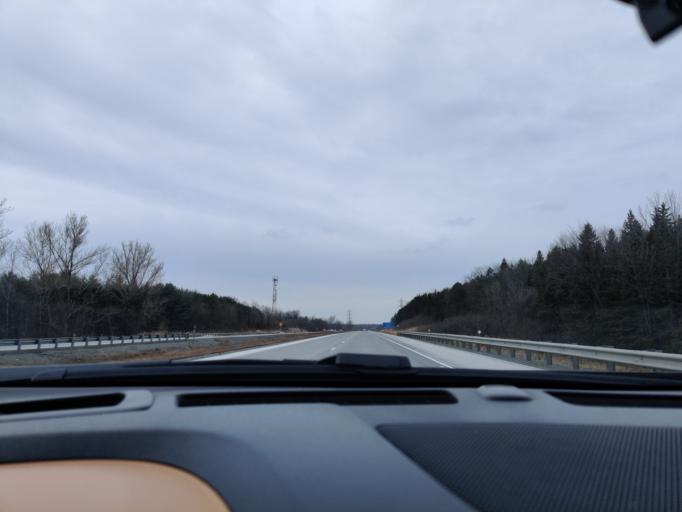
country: CA
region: Ontario
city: Cornwall
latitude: 45.0659
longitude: -74.6600
